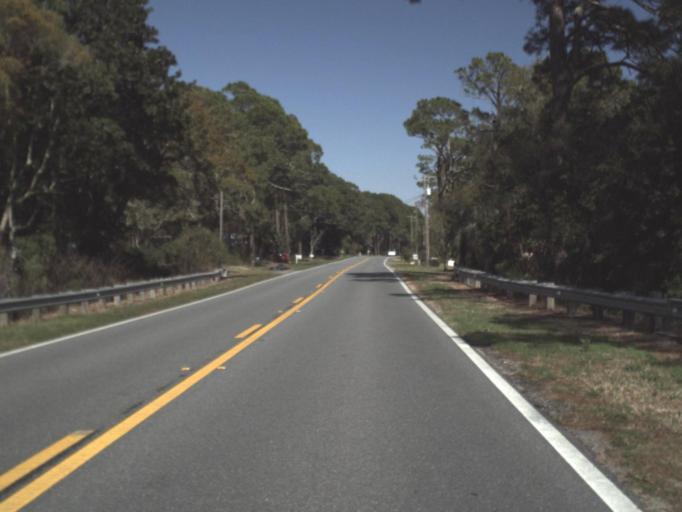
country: US
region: Florida
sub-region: Franklin County
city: Carrabelle
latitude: 29.9045
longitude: -84.5470
